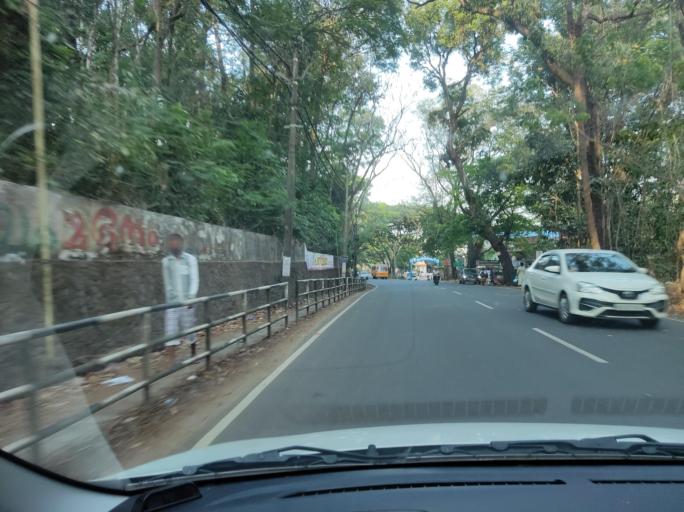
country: IN
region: Kerala
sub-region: Kottayam
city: Kottayam
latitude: 9.6341
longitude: 76.5251
